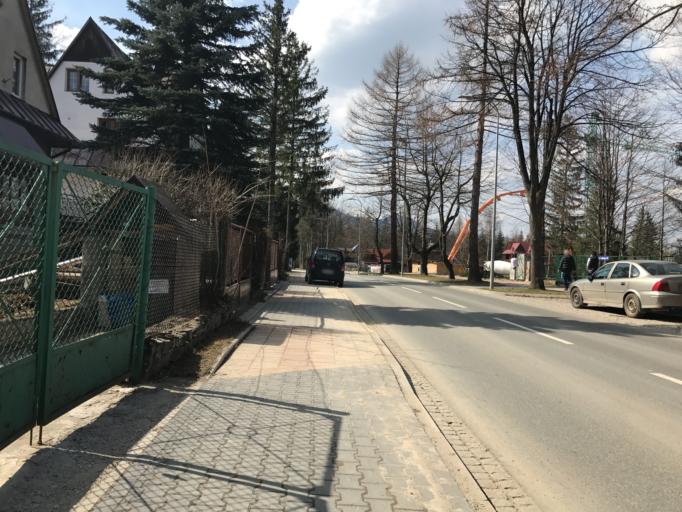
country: PL
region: Lesser Poland Voivodeship
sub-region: Powiat tatrzanski
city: Zakopane
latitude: 49.2871
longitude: 19.9648
